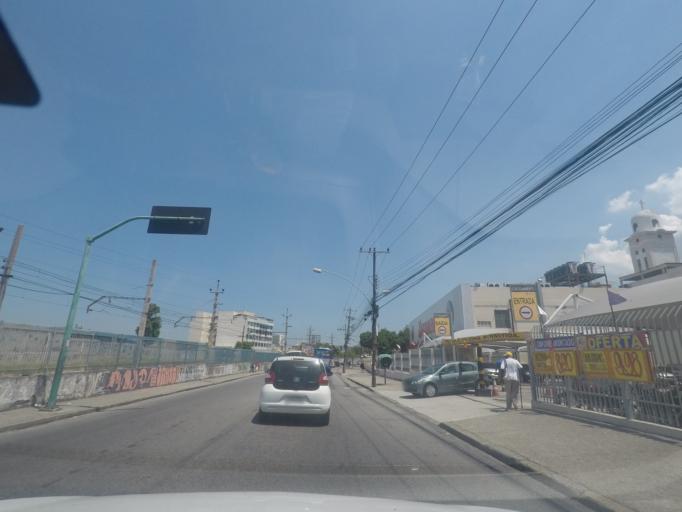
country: BR
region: Rio de Janeiro
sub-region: Rio De Janeiro
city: Rio de Janeiro
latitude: -22.8558
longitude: -43.2598
